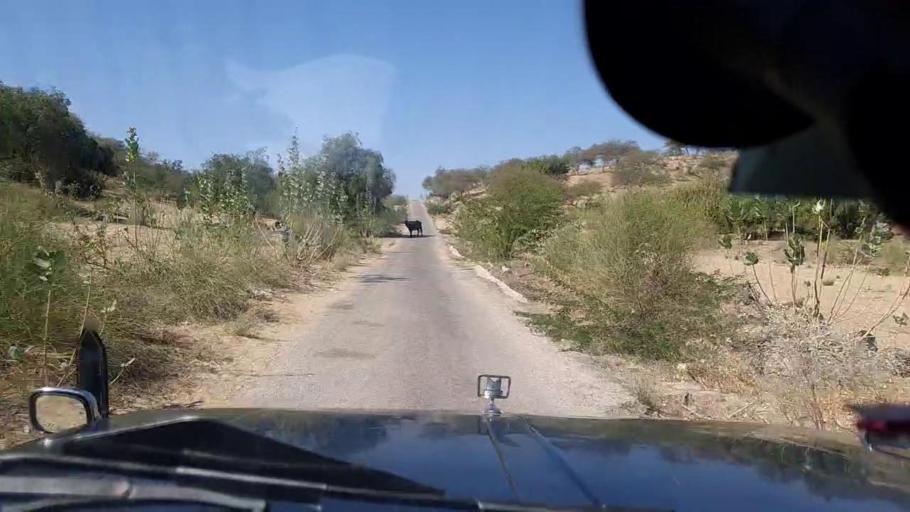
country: PK
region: Sindh
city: Mithi
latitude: 24.6120
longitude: 69.7121
